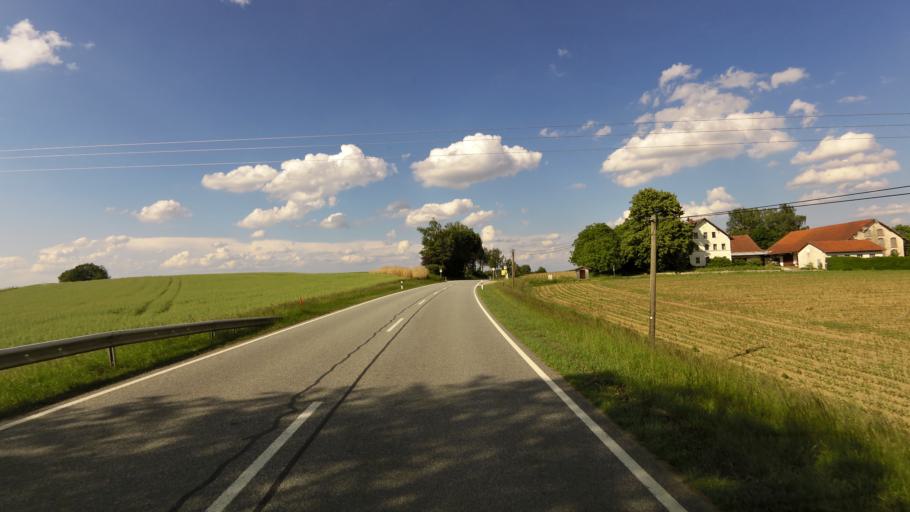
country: DE
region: Bavaria
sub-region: Lower Bavaria
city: Vilsheim
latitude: 48.4222
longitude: 12.1304
